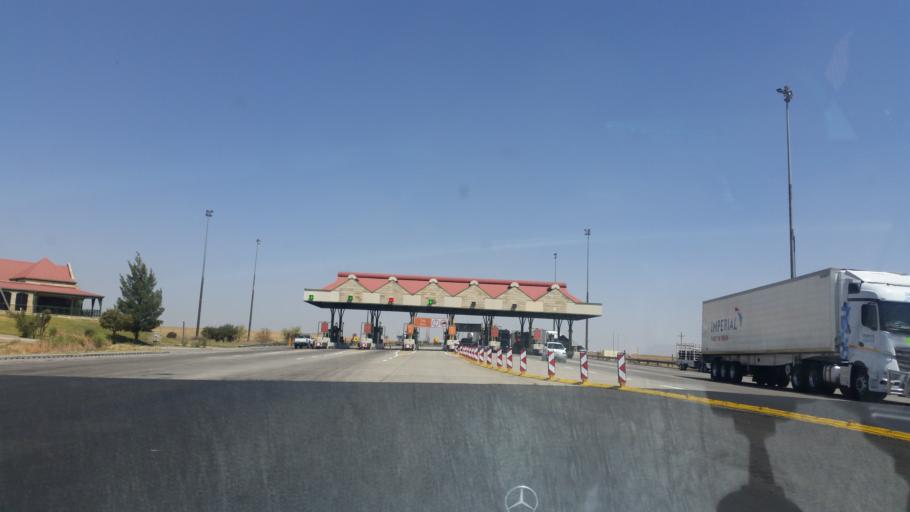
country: ZA
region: Orange Free State
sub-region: Lejweleputswa District Municipality
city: Brandfort
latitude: -28.7982
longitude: 26.6913
